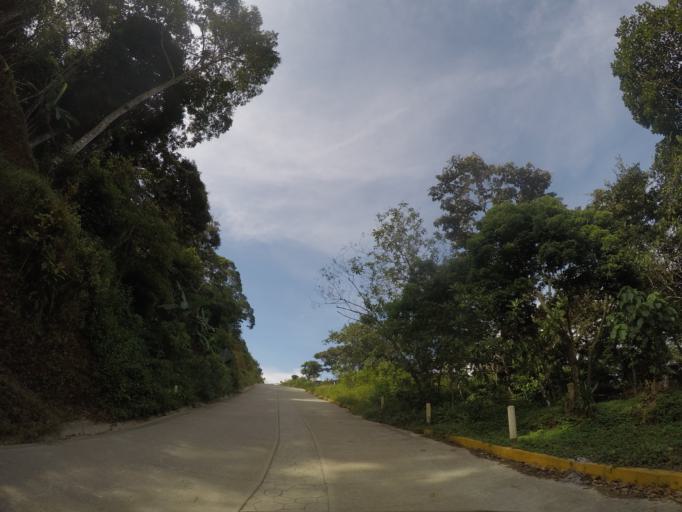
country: MX
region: Oaxaca
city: Pluma Hidalgo
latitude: 15.9306
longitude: -96.4175
